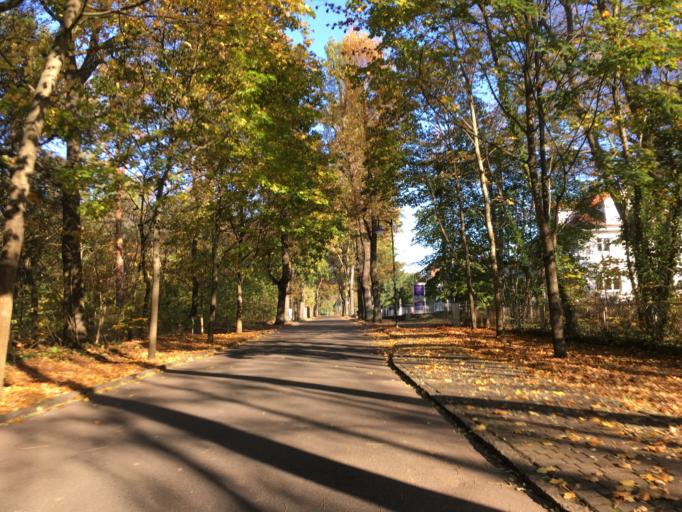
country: DE
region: Brandenburg
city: Bad Saarow
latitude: 52.2692
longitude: 14.0637
